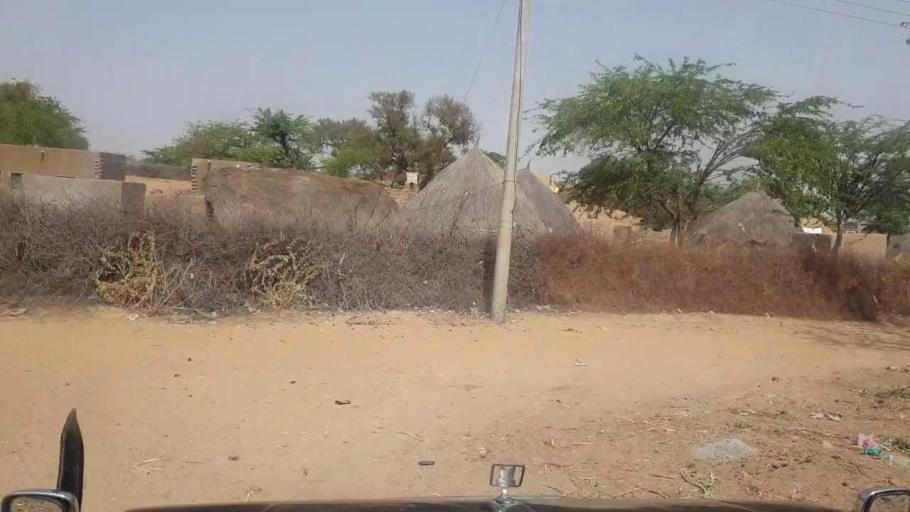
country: PK
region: Sindh
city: Islamkot
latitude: 25.0999
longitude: 70.1756
